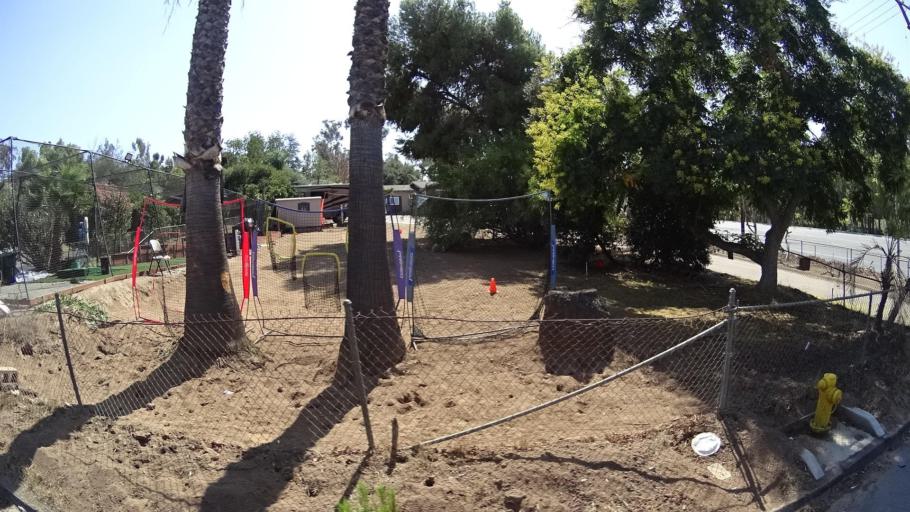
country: US
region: California
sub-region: San Diego County
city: Bostonia
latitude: 32.7793
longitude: -116.9274
